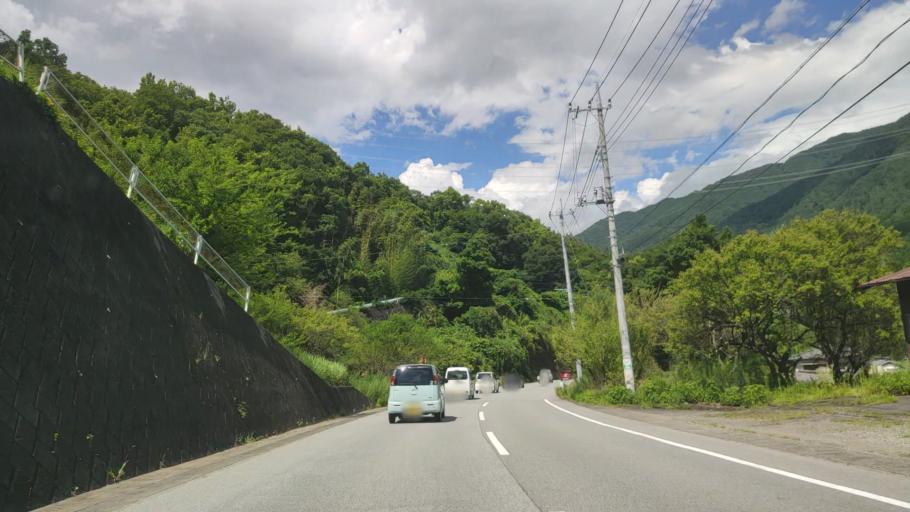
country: JP
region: Yamanashi
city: Enzan
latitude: 35.7580
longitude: 138.7275
